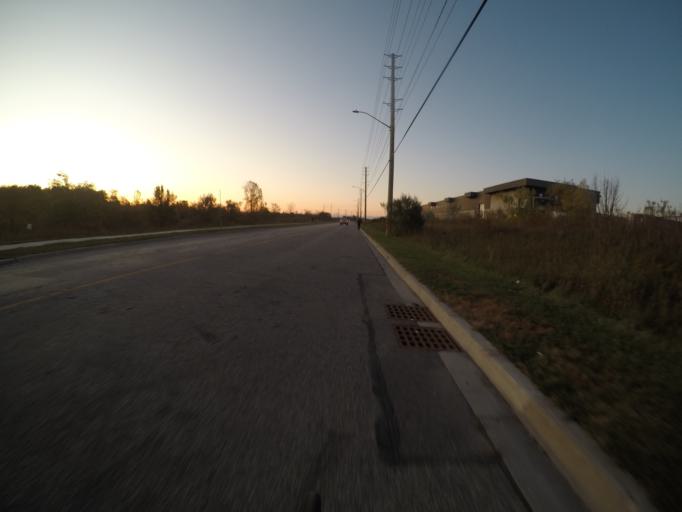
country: CA
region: Ontario
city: Kitchener
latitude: 43.4183
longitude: -80.4345
